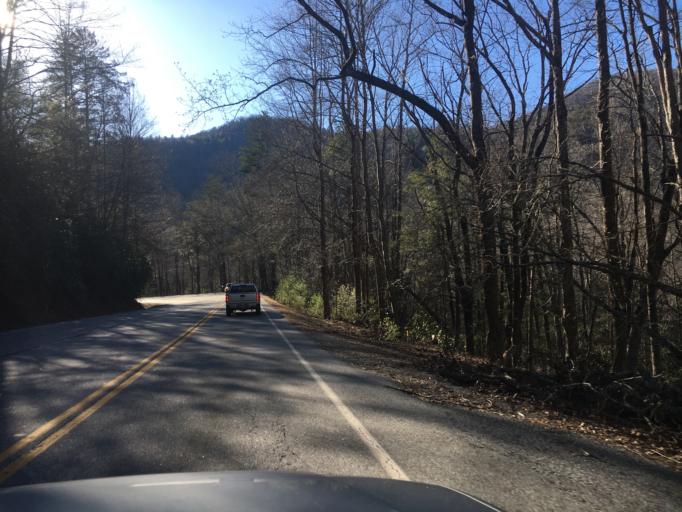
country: US
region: Georgia
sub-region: Union County
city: Blairsville
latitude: 34.7081
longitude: -83.9124
